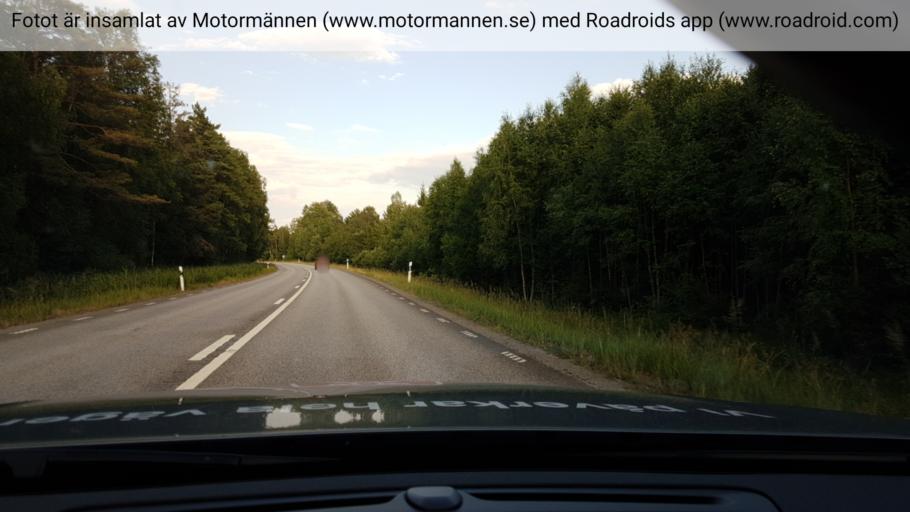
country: SE
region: Uppsala
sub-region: Enkopings Kommun
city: Orsundsbro
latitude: 59.8901
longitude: 17.1721
